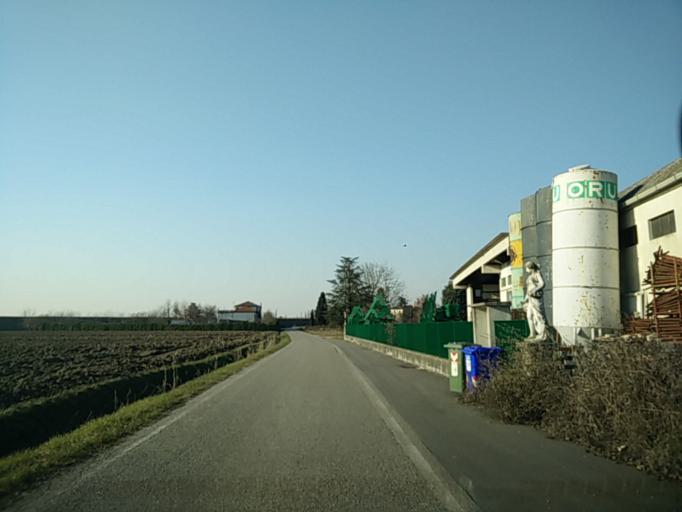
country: IT
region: Veneto
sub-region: Provincia di Venezia
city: Torre di Mosto
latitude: 45.6850
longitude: 12.7284
